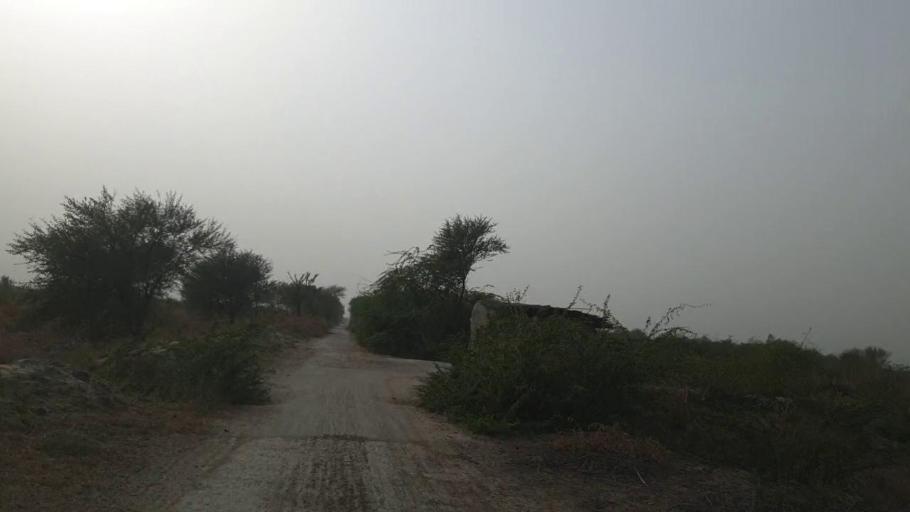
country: PK
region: Sindh
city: Kunri
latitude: 25.0677
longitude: 69.4882
